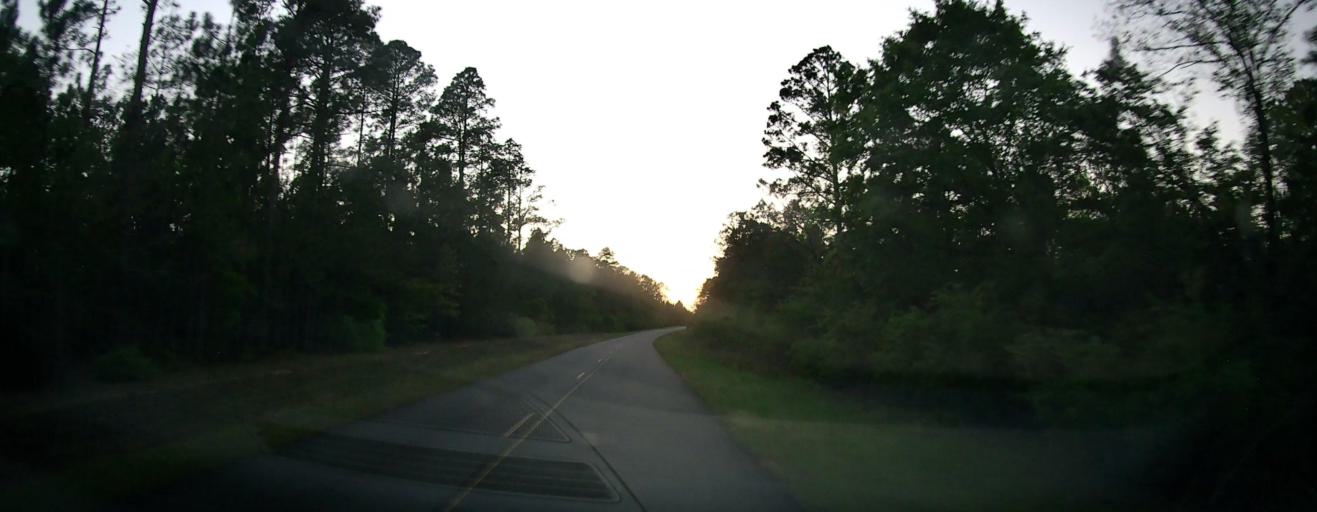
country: US
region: Georgia
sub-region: Marion County
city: Buena Vista
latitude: 32.2543
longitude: -84.6168
